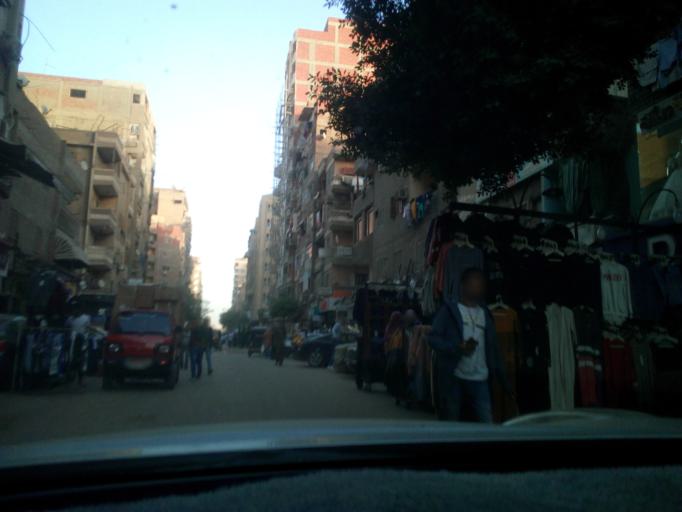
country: EG
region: Muhafazat al Qalyubiyah
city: Al Khankah
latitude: 30.1286
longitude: 31.3476
